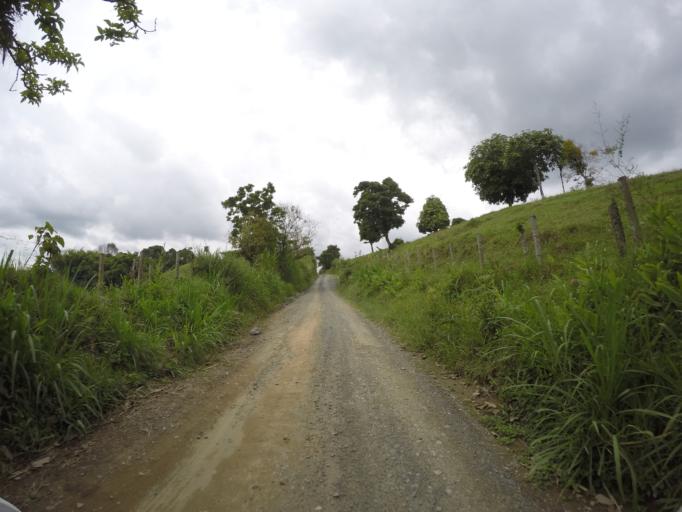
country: CO
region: Quindio
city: Filandia
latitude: 4.6347
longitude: -75.6836
